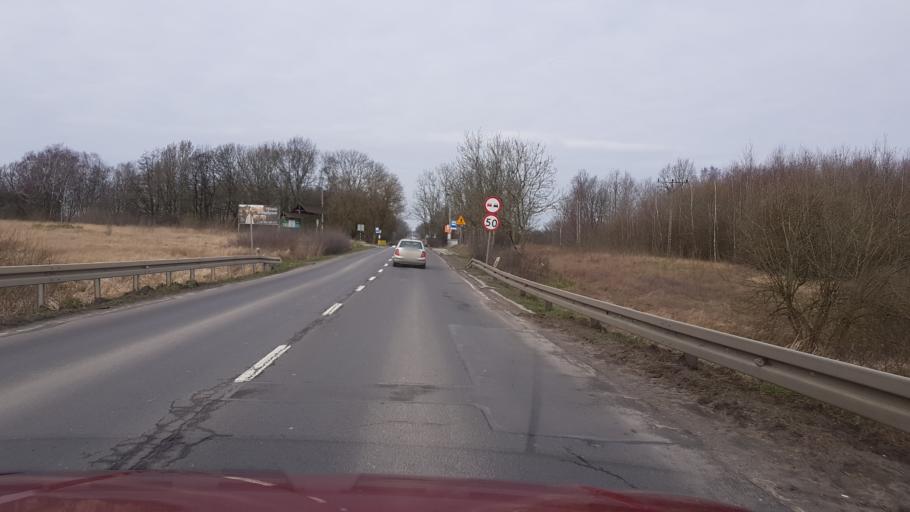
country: PL
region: West Pomeranian Voivodeship
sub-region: Powiat policki
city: Police
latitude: 53.5005
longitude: 14.5787
